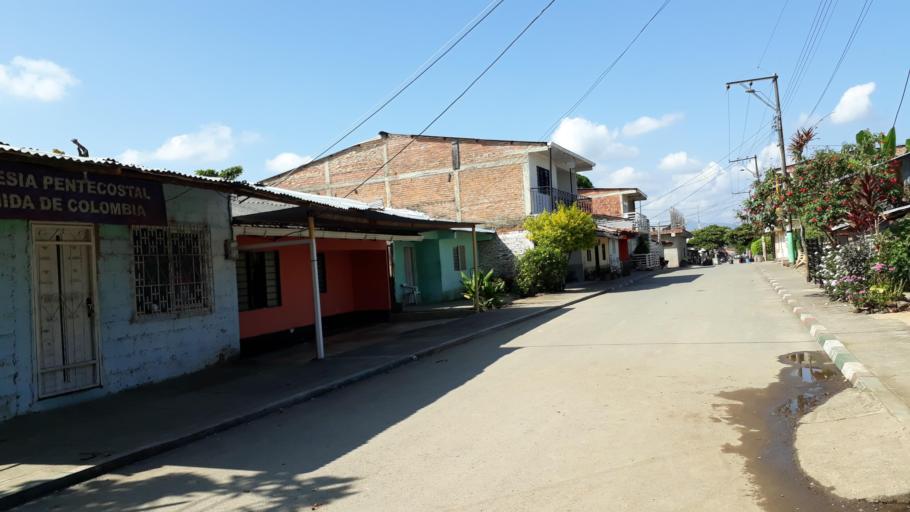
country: CO
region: Cauca
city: Buenos Aires
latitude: 3.1244
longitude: -76.6225
